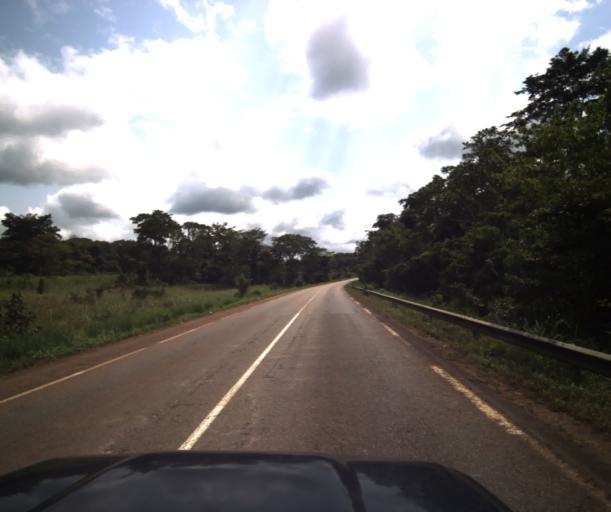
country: CM
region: Centre
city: Eseka
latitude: 3.8728
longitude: 10.6239
